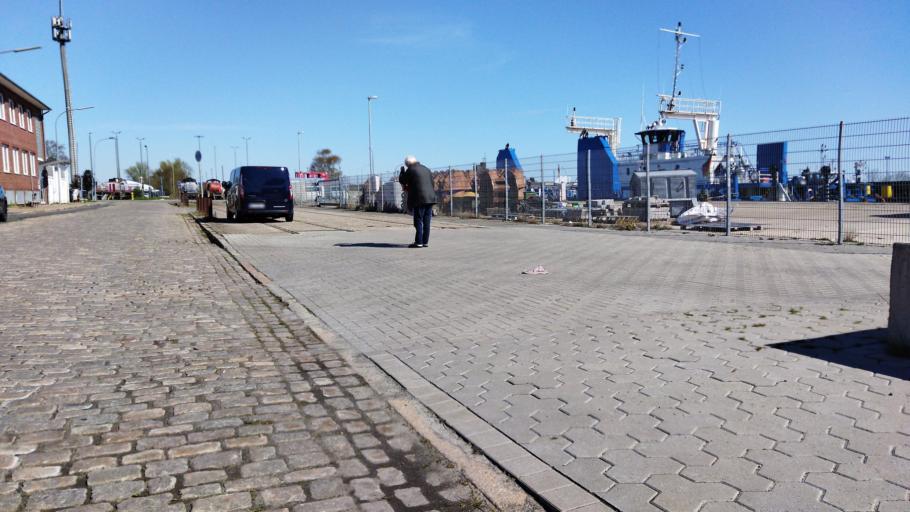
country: DE
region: Bremen
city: Bremerhaven
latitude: 53.5677
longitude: 8.5602
